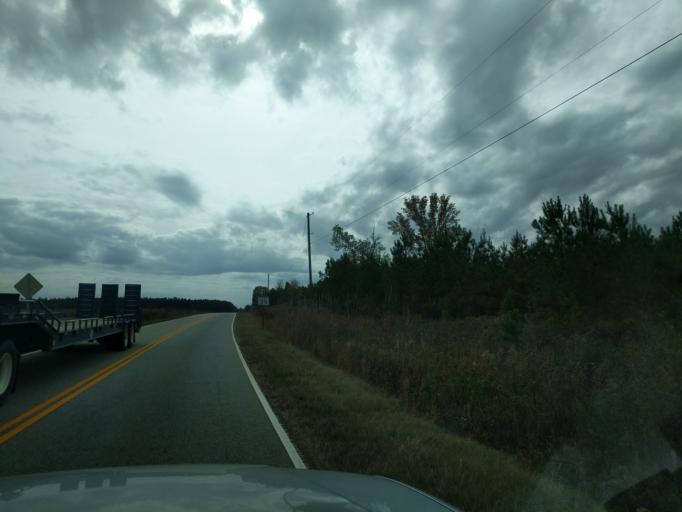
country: US
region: South Carolina
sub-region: Saluda County
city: Saluda
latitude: 34.1112
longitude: -81.8311
